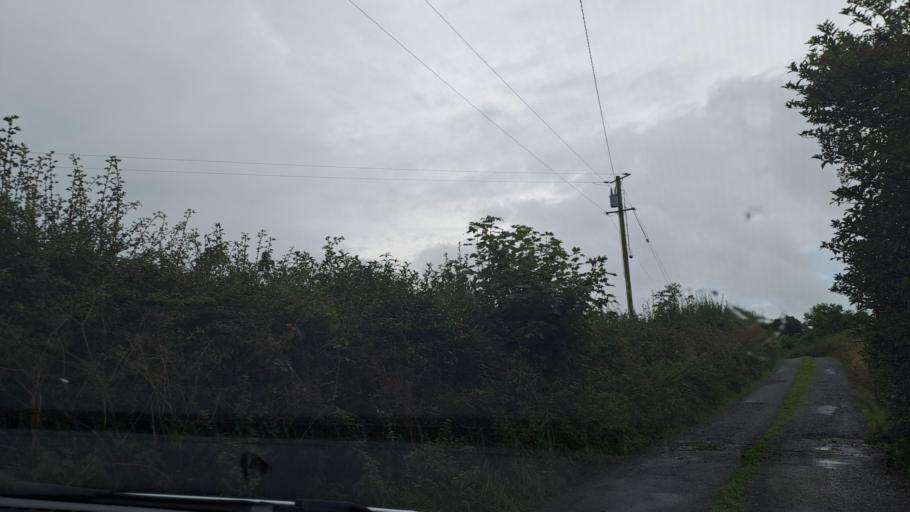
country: IE
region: Ulster
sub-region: An Cabhan
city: Kingscourt
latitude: 53.9741
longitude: -6.8475
